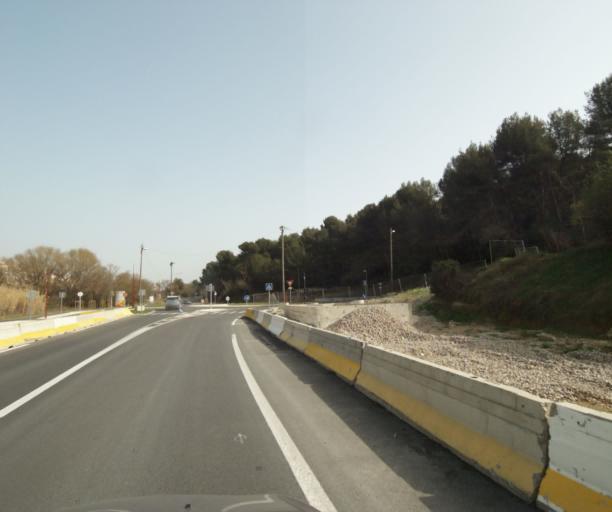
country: FR
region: Provence-Alpes-Cote d'Azur
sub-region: Departement des Bouches-du-Rhone
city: Les Pennes-Mirabeau
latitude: 43.4077
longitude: 5.3012
